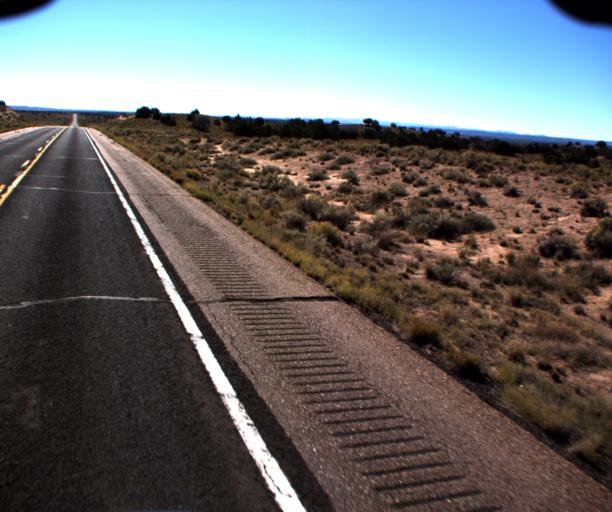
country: US
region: Arizona
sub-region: Navajo County
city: Snowflake
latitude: 34.6755
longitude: -109.7294
